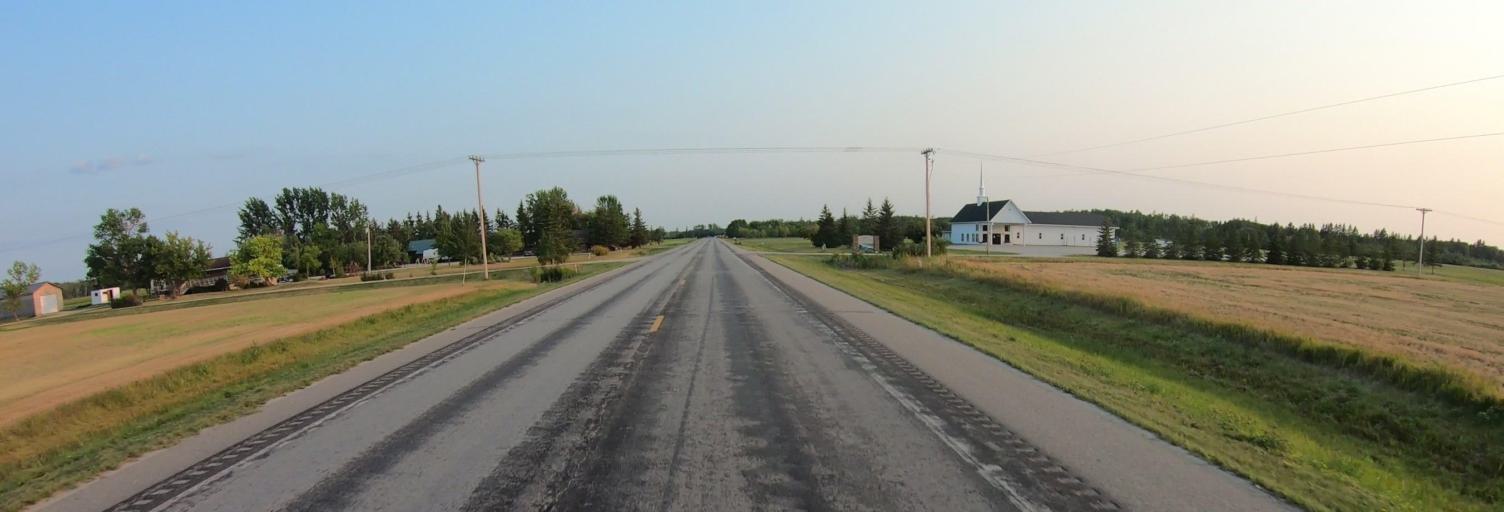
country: US
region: Minnesota
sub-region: Roseau County
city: Warroad
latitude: 48.8949
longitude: -95.3201
